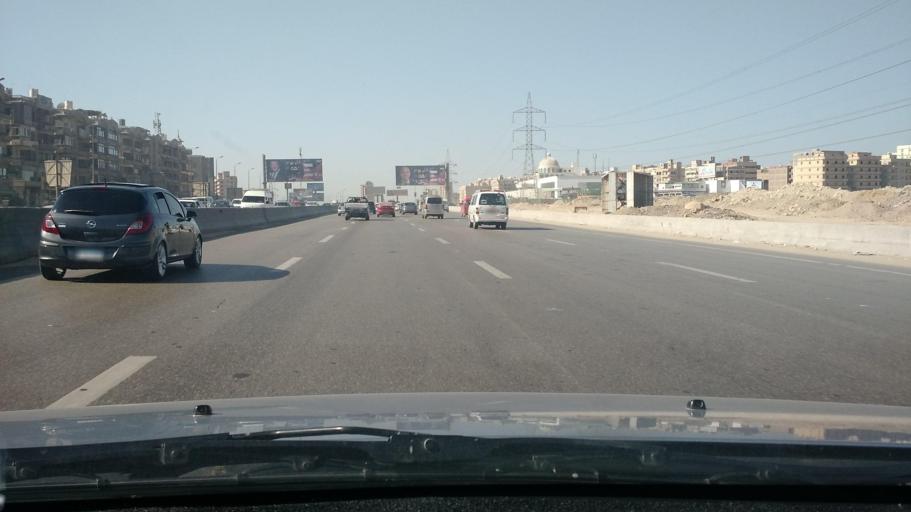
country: EG
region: Muhafazat al Qahirah
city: Cairo
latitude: 29.9854
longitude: 31.3130
